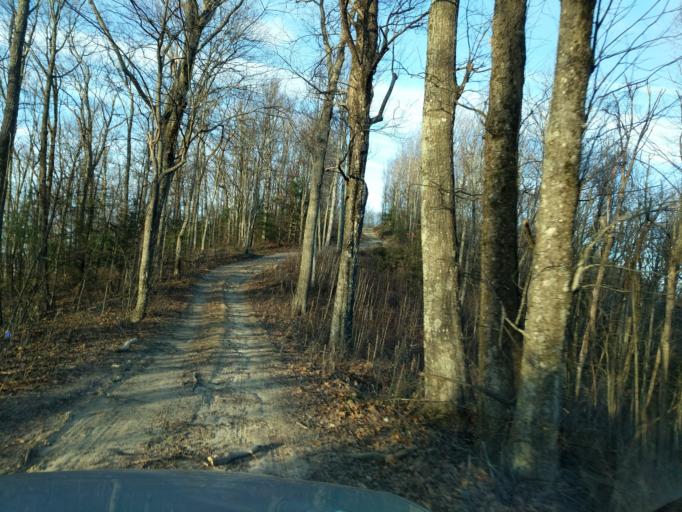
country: US
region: North Carolina
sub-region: Haywood County
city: Cove Creek
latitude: 35.7300
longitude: -83.0535
